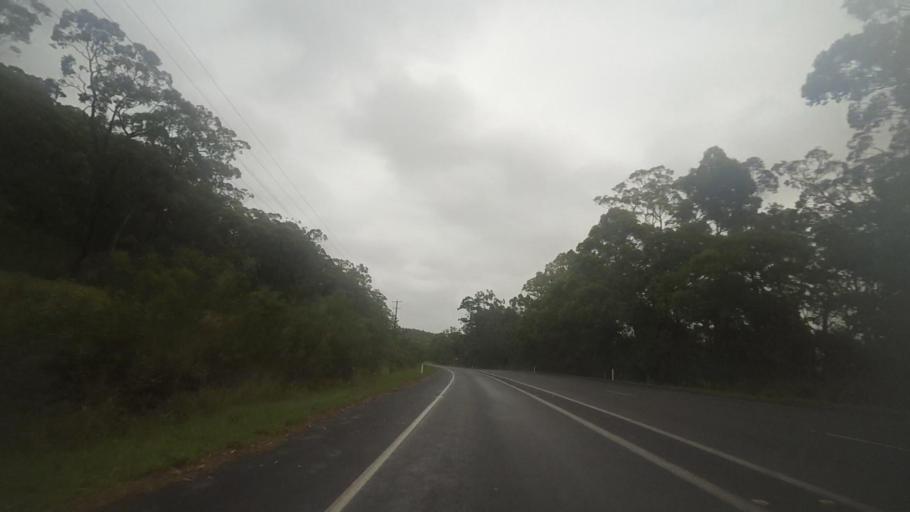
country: AU
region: New South Wales
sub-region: Port Stephens Shire
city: Port Stephens
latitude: -32.6446
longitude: 151.9836
